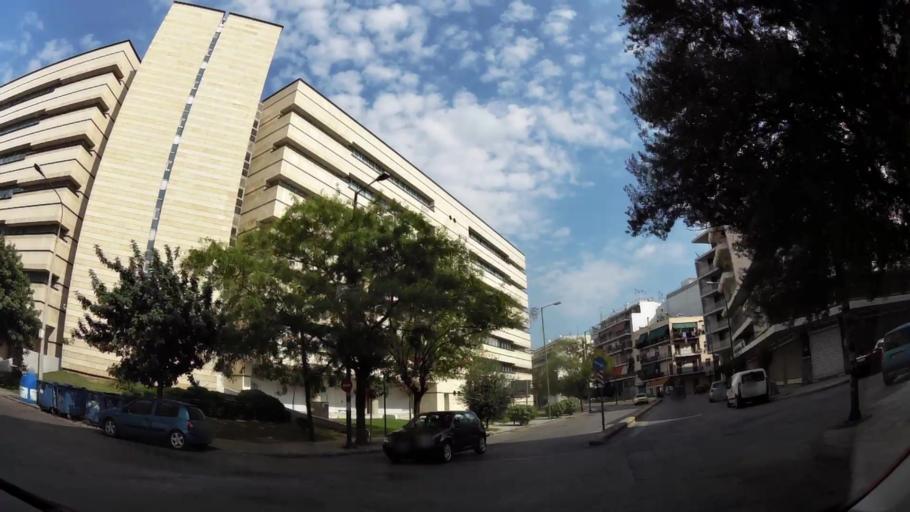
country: GR
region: Attica
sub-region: Nomarchia Athinas
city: Nea Smyrni
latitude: 37.9578
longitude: 23.7198
